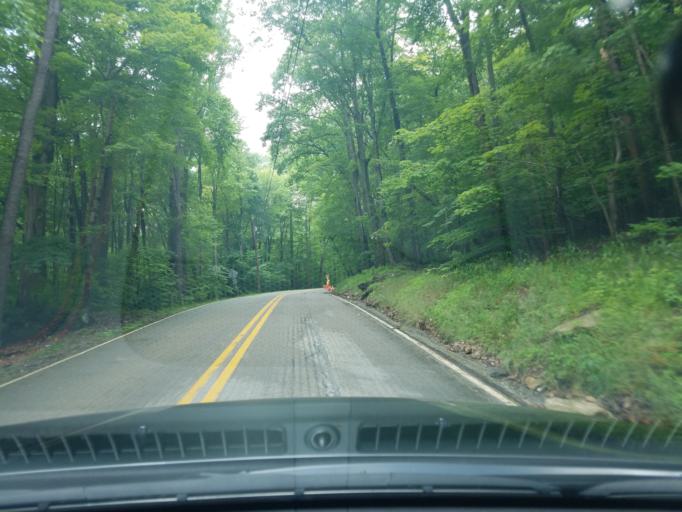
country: US
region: Pennsylvania
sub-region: Fayette County
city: Bear Rocks
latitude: 40.1801
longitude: -79.3697
